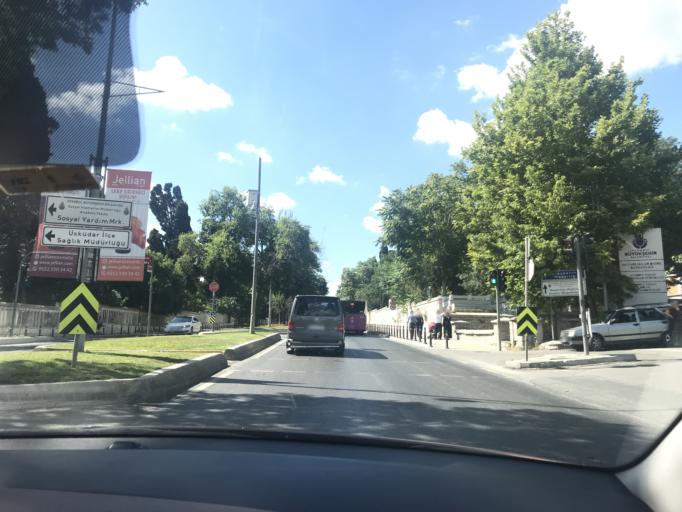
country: TR
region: Istanbul
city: UEskuedar
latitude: 41.0090
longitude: 29.0230
